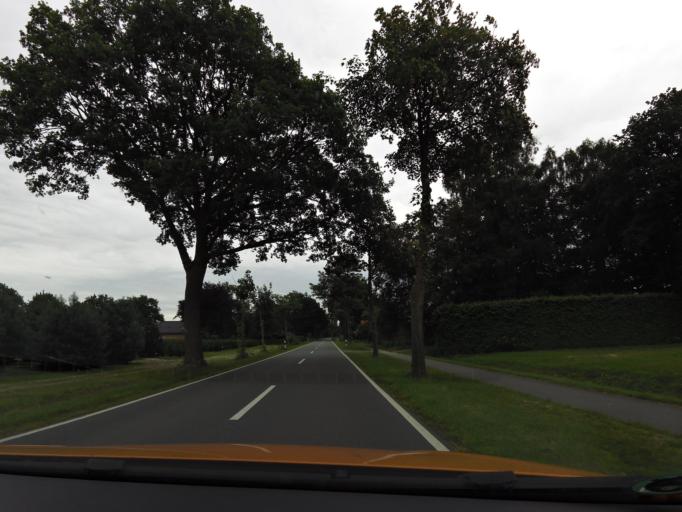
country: DE
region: Lower Saxony
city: Wiefelstede
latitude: 53.1950
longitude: 8.1363
